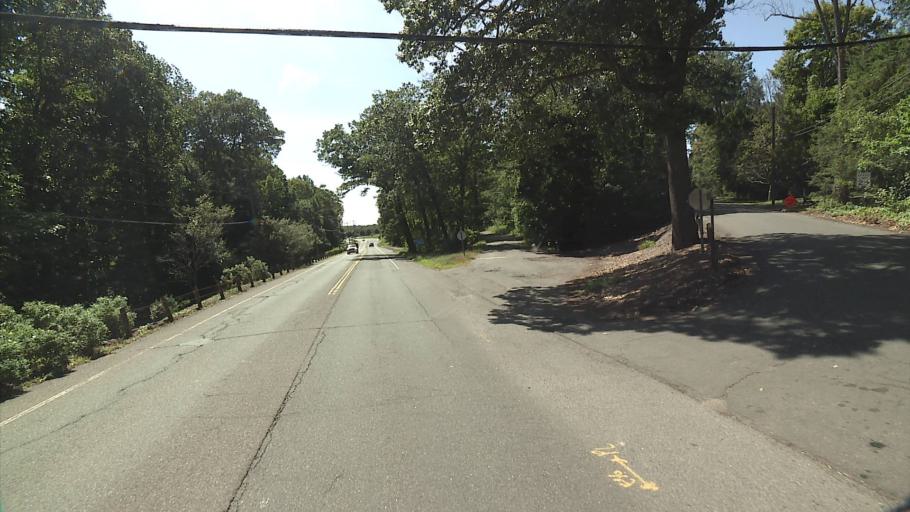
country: US
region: Connecticut
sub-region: New Haven County
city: Middlebury
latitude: 41.5249
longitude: -73.1326
